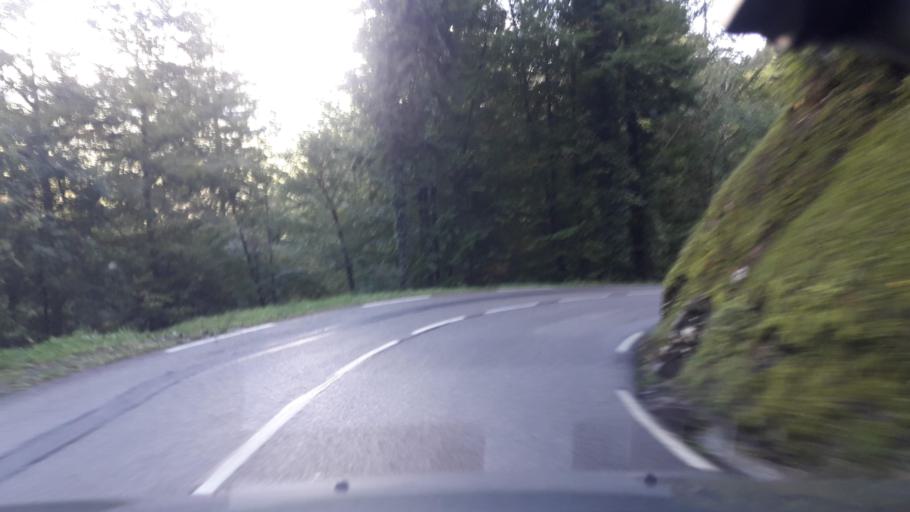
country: FR
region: Rhone-Alpes
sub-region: Departement de la Savoie
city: Les Echelles
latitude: 45.4173
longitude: 5.8428
